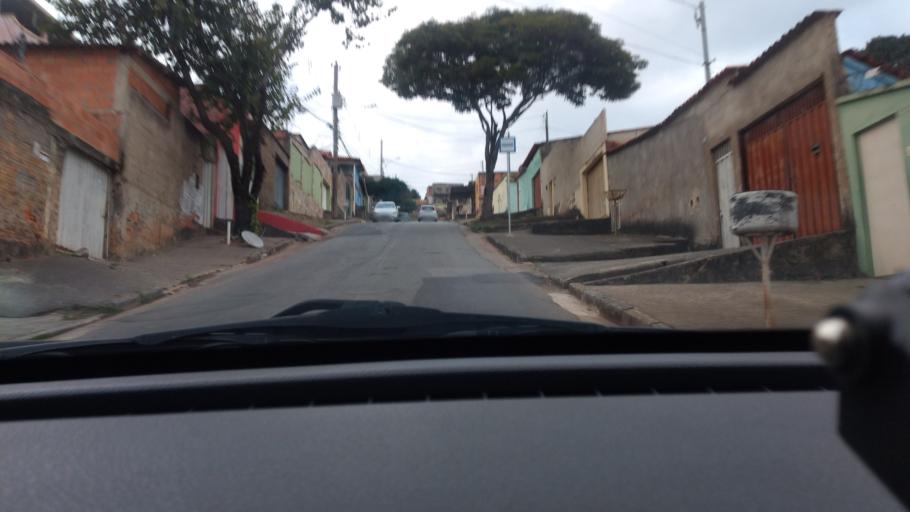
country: BR
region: Minas Gerais
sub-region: Santa Luzia
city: Santa Luzia
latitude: -19.8164
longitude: -43.9371
